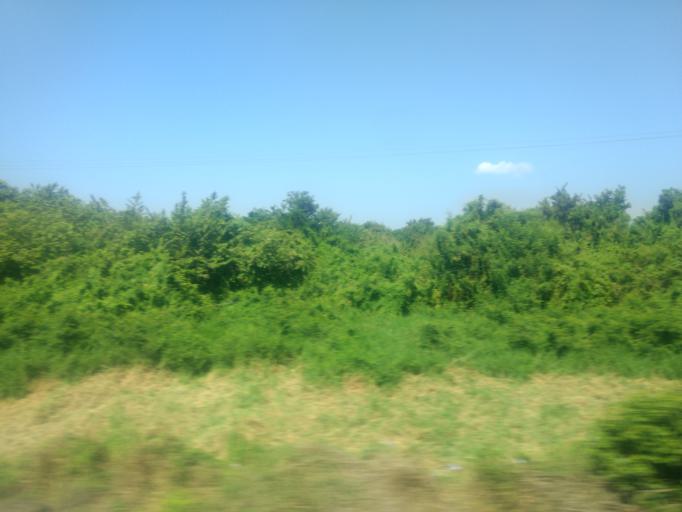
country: MX
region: Colima
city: El Colomo
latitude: 19.0446
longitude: -104.2610
